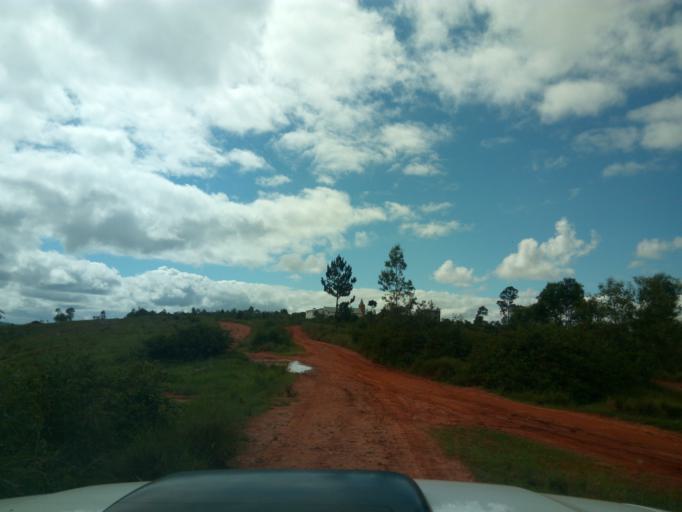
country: MG
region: Analamanga
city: Antananarivo
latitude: -18.7306
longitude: 47.4130
